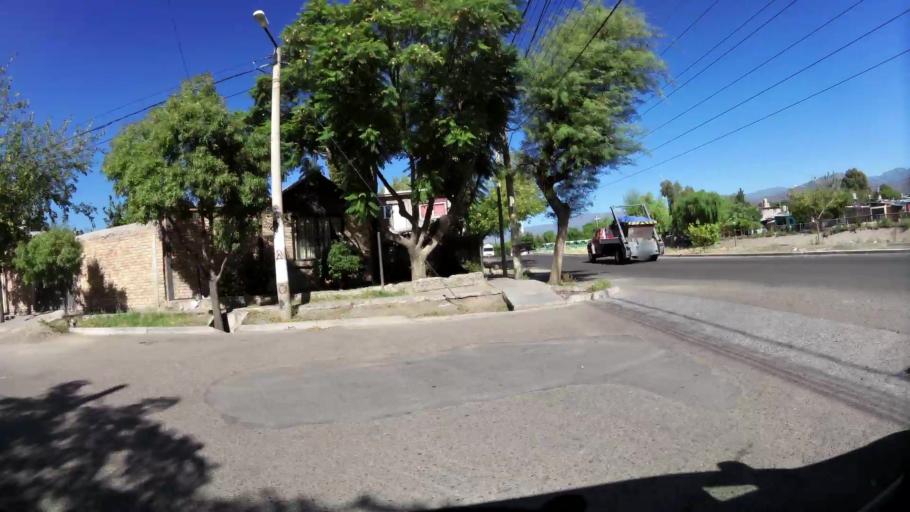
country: AR
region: Mendoza
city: Las Heras
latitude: -32.8723
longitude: -68.8677
